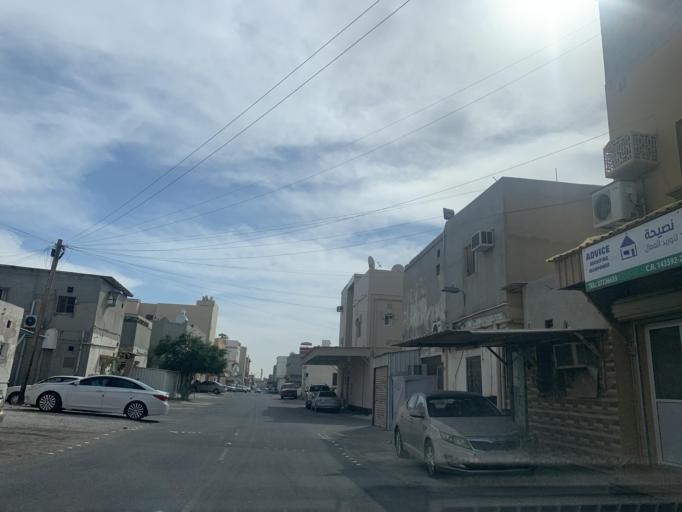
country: BH
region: Central Governorate
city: Madinat Hamad
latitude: 26.1208
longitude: 50.4797
